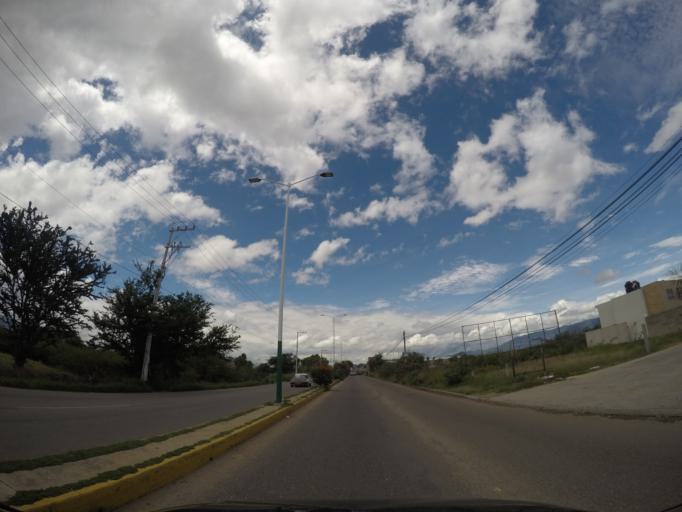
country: MX
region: Oaxaca
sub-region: Santa Cruz Xoxocotlan
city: San Isidro Monjas
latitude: 17.0086
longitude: -96.7365
